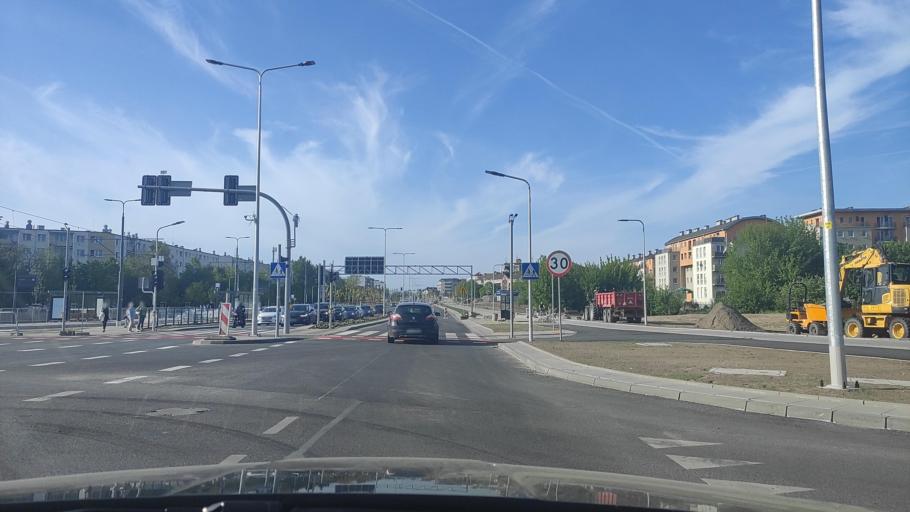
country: PL
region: Greater Poland Voivodeship
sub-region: Powiat poznanski
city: Czerwonak
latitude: 52.4474
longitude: 16.9456
